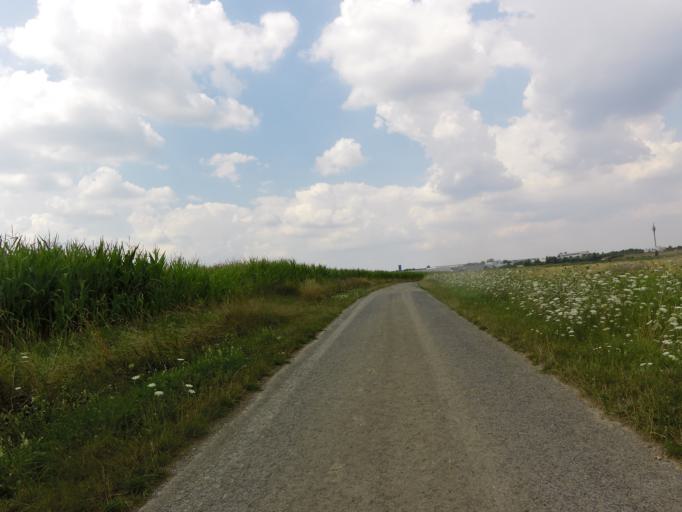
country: DE
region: Bavaria
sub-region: Regierungsbezirk Unterfranken
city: Eibelstadt
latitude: 49.7277
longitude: 9.9747
